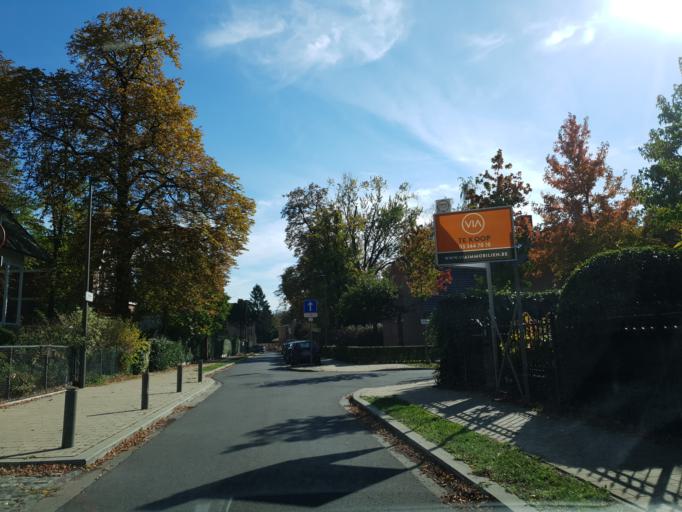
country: BE
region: Flanders
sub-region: Provincie Antwerpen
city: Kapellen
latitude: 51.2869
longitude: 4.4379
